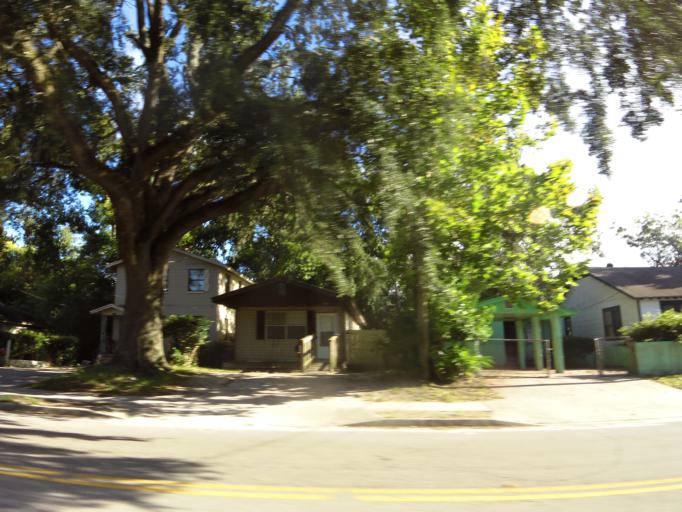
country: US
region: Florida
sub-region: Duval County
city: Jacksonville
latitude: 30.3513
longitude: -81.6923
